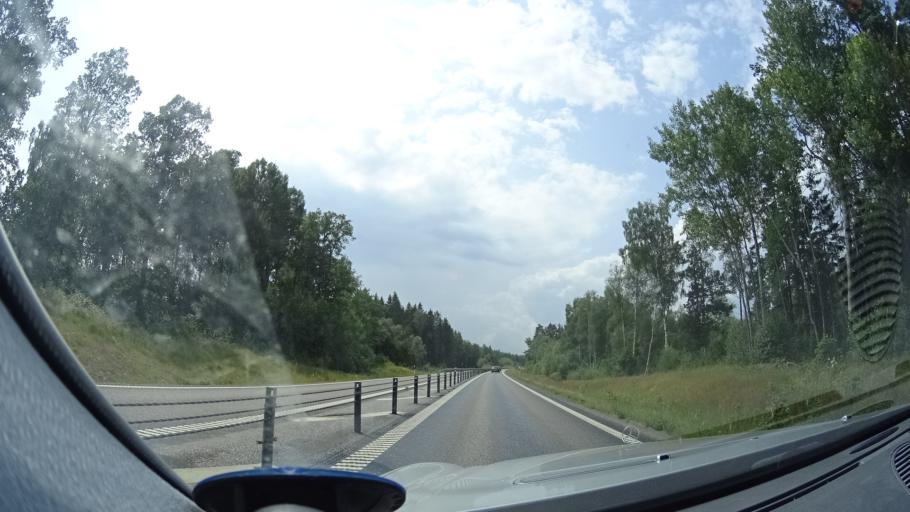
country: SE
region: Kalmar
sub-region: Nybro Kommun
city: Nybro
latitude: 56.7290
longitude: 15.8333
